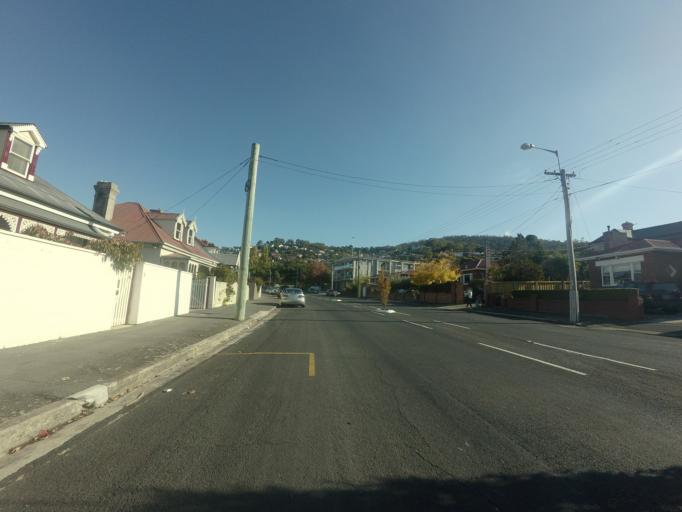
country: AU
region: Tasmania
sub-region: Hobart
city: Hobart
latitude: -42.8799
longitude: 147.3108
